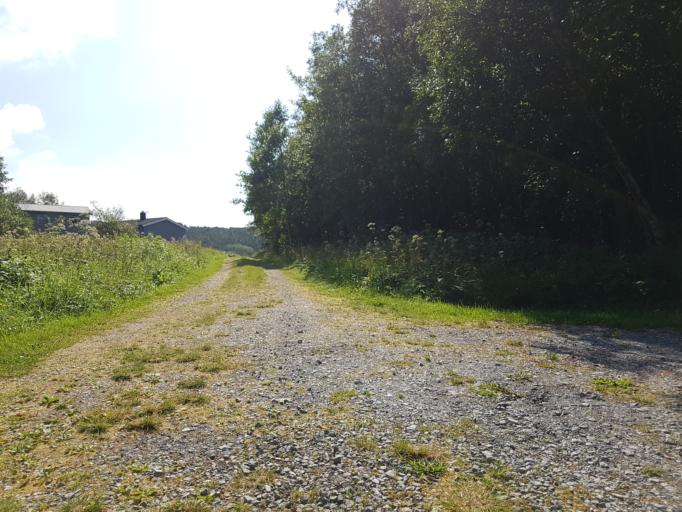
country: NO
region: Sor-Trondelag
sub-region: Agdenes
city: Lensvik
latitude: 63.6336
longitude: 9.8411
